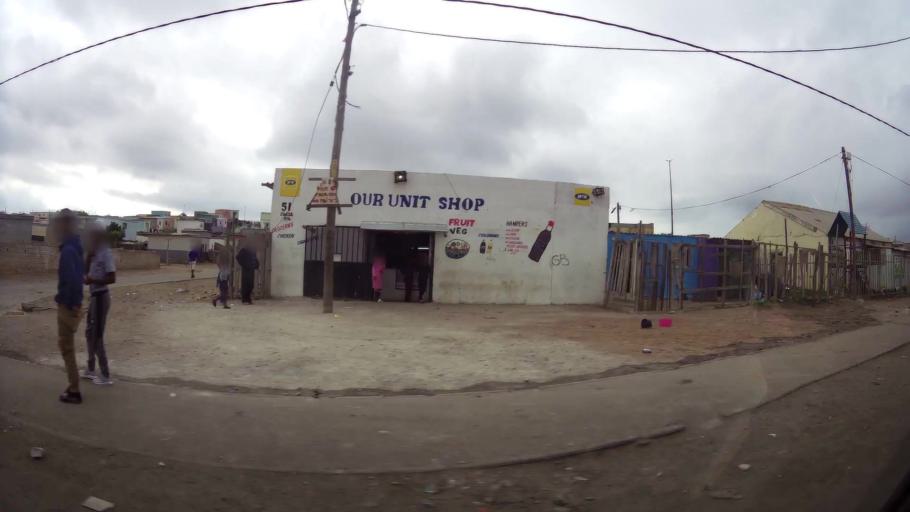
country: ZA
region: Eastern Cape
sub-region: Nelson Mandela Bay Metropolitan Municipality
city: Port Elizabeth
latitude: -33.8835
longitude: 25.5560
